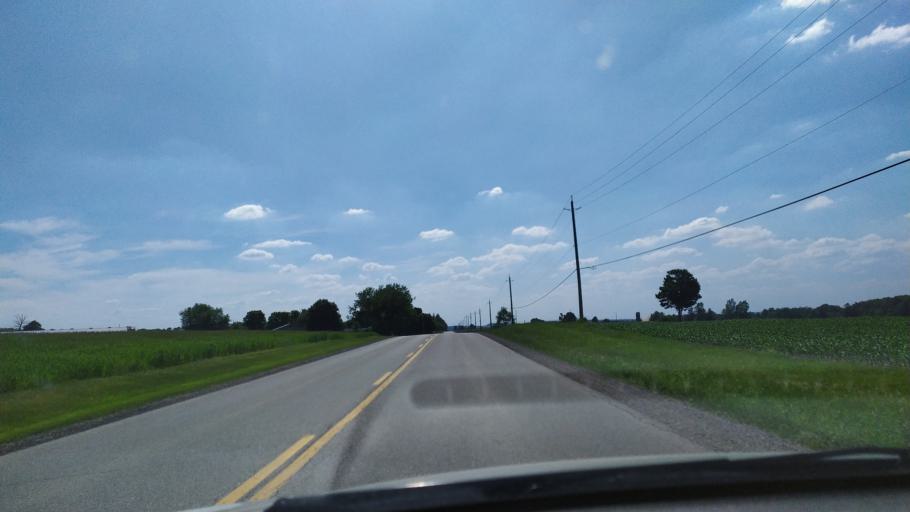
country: CA
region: Ontario
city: Kitchener
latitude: 43.3650
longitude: -80.5993
